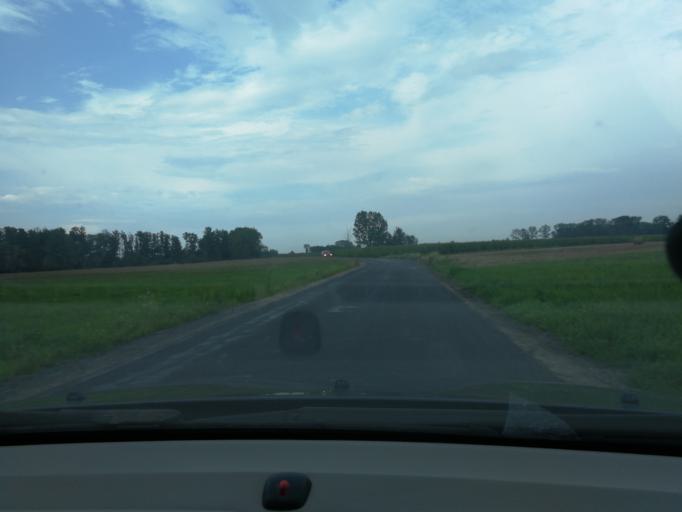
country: PL
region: Masovian Voivodeship
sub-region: Powiat warszawski zachodni
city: Bieniewice
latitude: 52.1151
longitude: 20.5562
